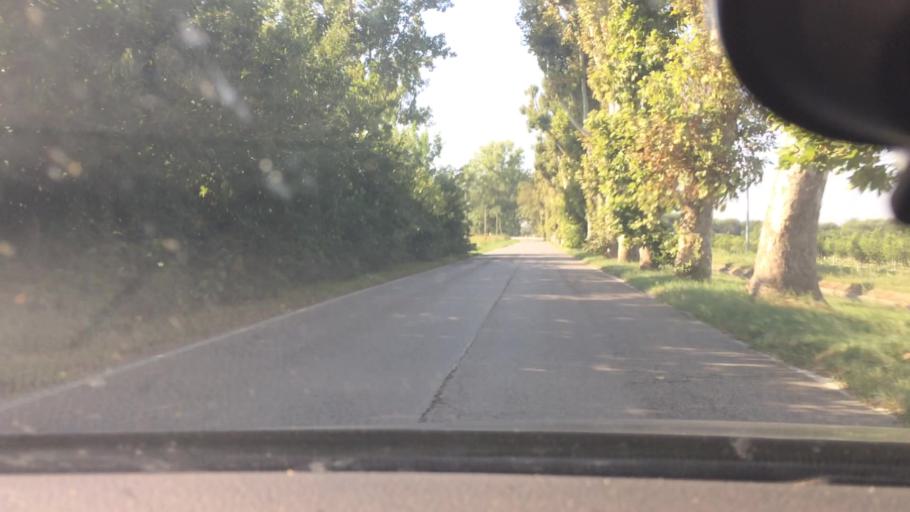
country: IT
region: Emilia-Romagna
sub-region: Provincia di Ferrara
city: Lagosanto
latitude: 44.7505
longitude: 12.1368
